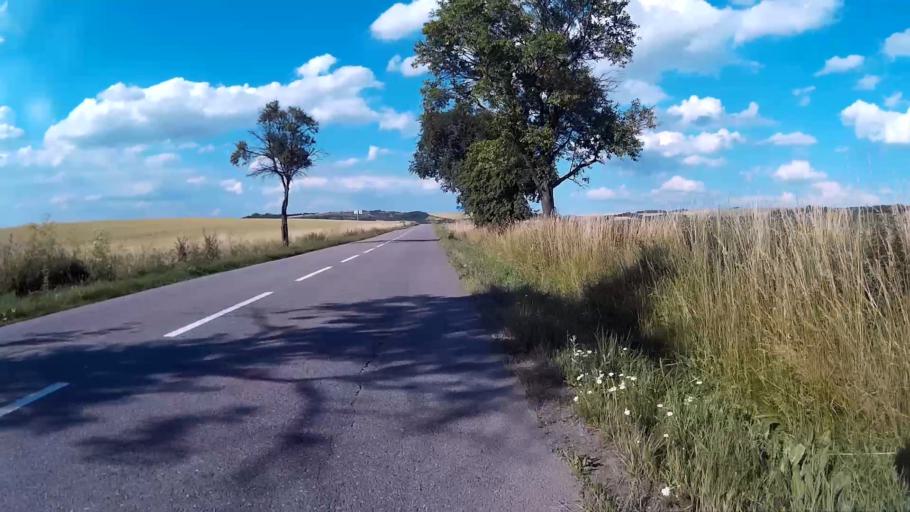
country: CZ
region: South Moravian
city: Sitborice
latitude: 49.0299
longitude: 16.7857
